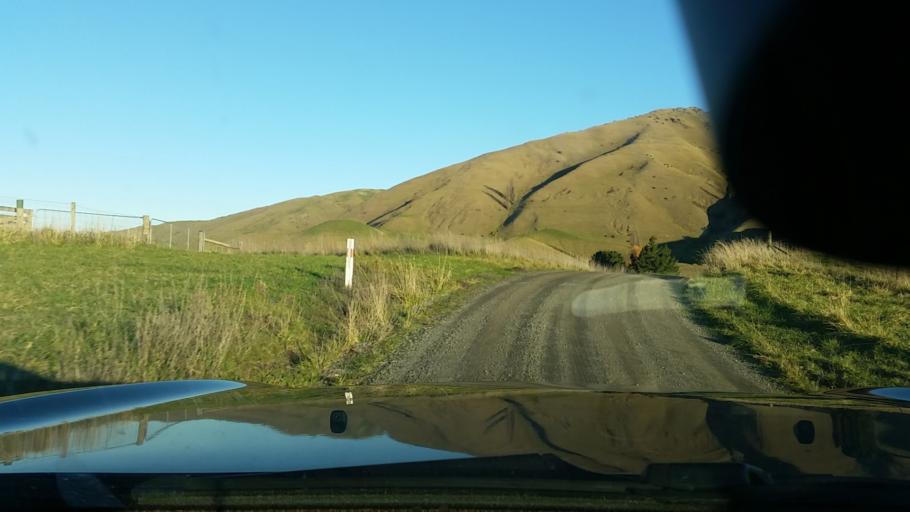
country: NZ
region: Marlborough
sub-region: Marlborough District
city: Blenheim
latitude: -41.7395
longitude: 174.0490
